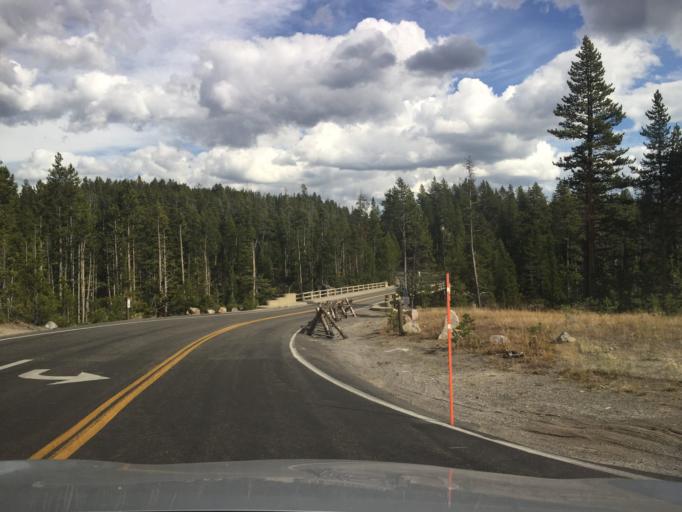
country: US
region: Montana
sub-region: Gallatin County
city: West Yellowstone
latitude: 44.7082
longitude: -110.5037
